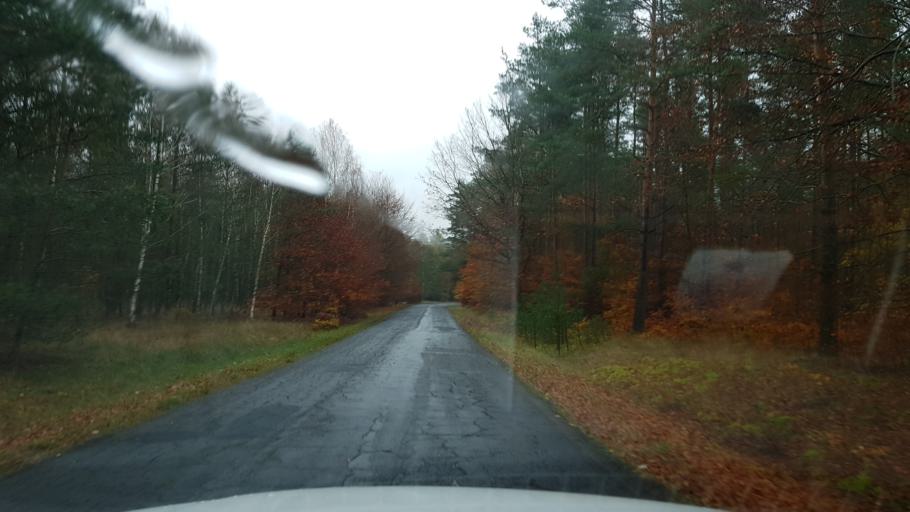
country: PL
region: West Pomeranian Voivodeship
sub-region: Powiat goleniowski
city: Stepnica
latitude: 53.6603
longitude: 14.7066
